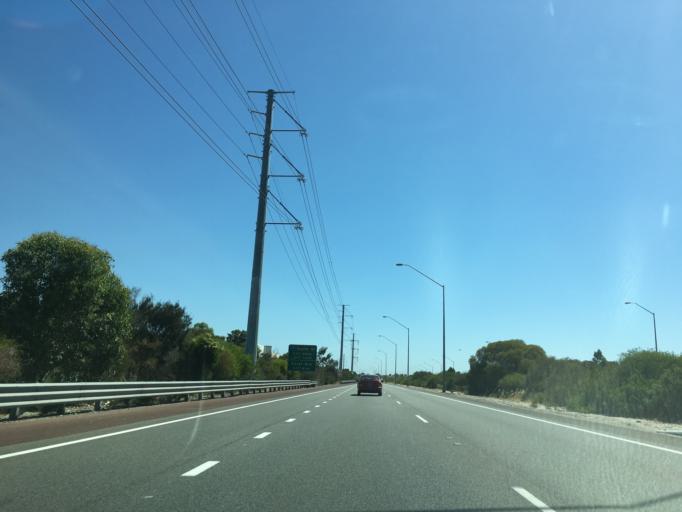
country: AU
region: Western Australia
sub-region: Canning
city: Willetton
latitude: -32.0611
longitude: 115.9001
